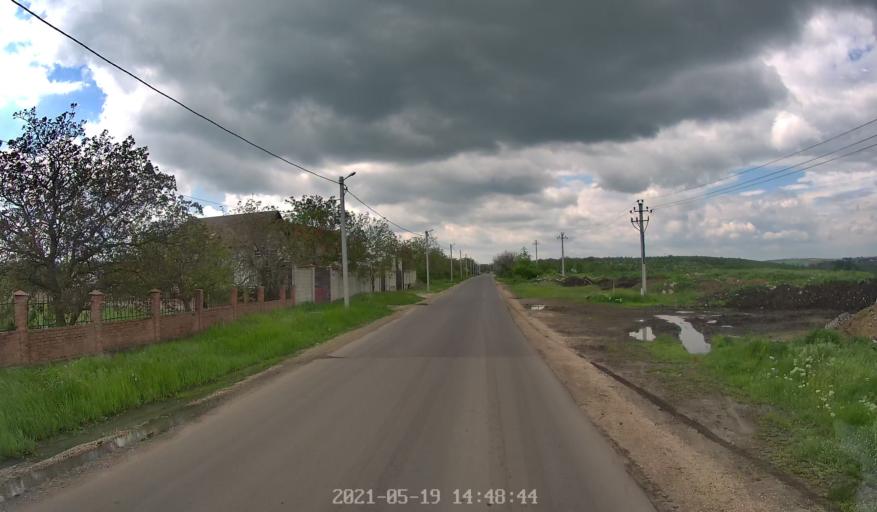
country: MD
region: Chisinau
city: Stauceni
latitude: 47.0460
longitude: 28.9583
